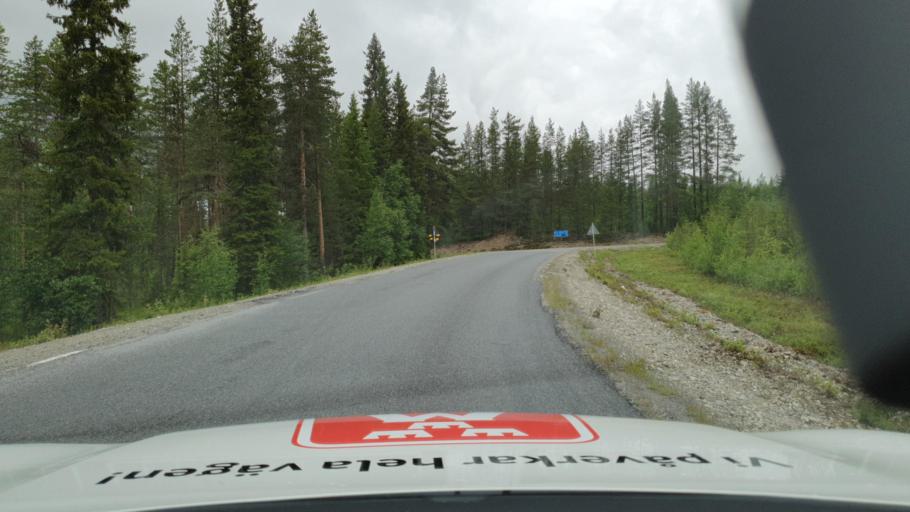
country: SE
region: Vaesterbotten
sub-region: Dorotea Kommun
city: Dorotea
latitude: 64.1887
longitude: 16.6143
